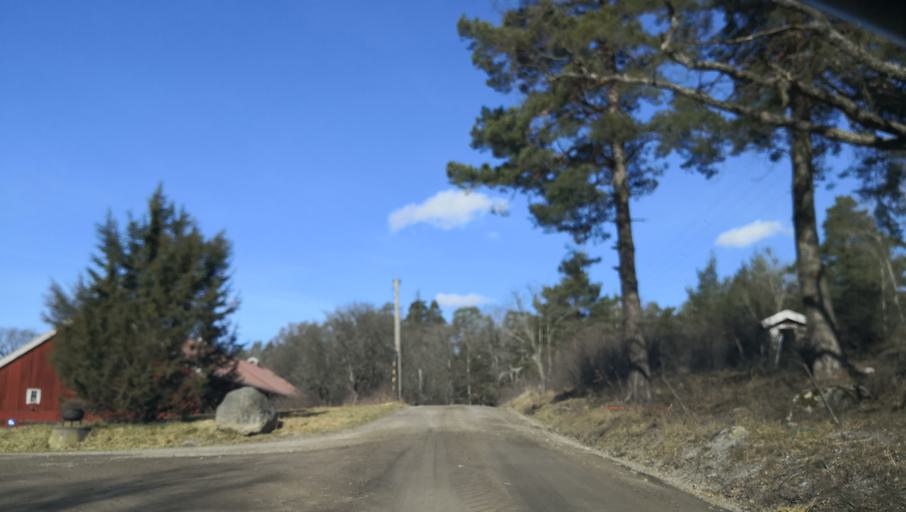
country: SE
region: Stockholm
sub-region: Varmdo Kommun
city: Gustavsberg
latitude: 59.2971
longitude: 18.3586
